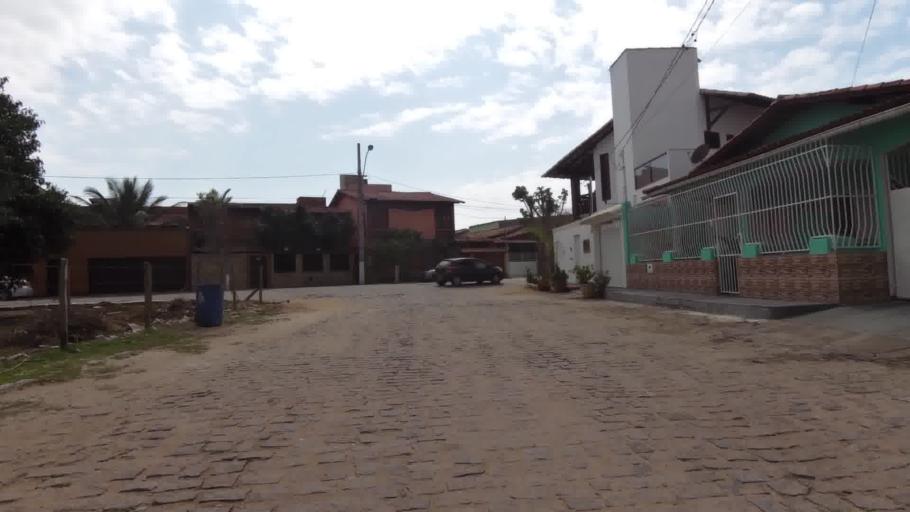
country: BR
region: Espirito Santo
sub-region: Marataizes
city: Marataizes
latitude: -21.0341
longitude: -40.8172
